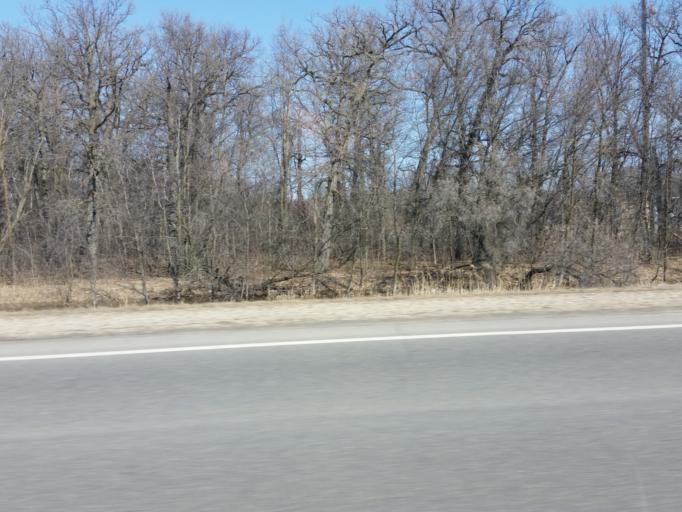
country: US
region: North Dakota
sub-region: Grand Forks County
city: Grand Forks
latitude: 48.0835
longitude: -97.1818
